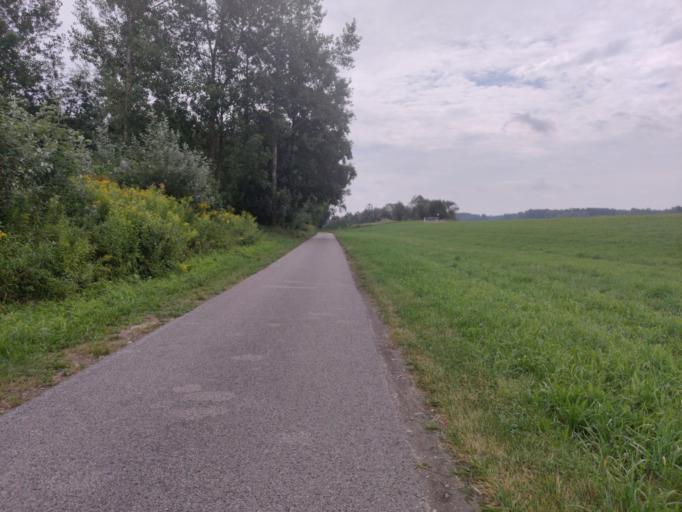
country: AT
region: Upper Austria
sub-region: Politischer Bezirk Perg
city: Perg
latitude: 48.2049
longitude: 14.6050
